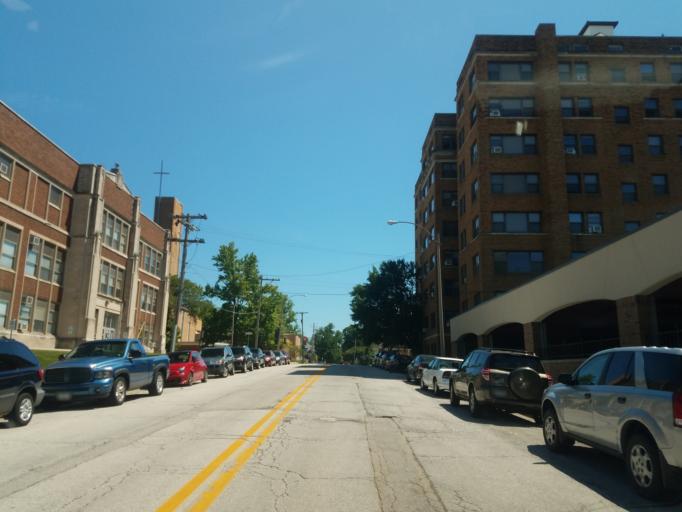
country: US
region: Illinois
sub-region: McLean County
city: Bloomington
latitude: 40.4803
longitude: -88.9886
